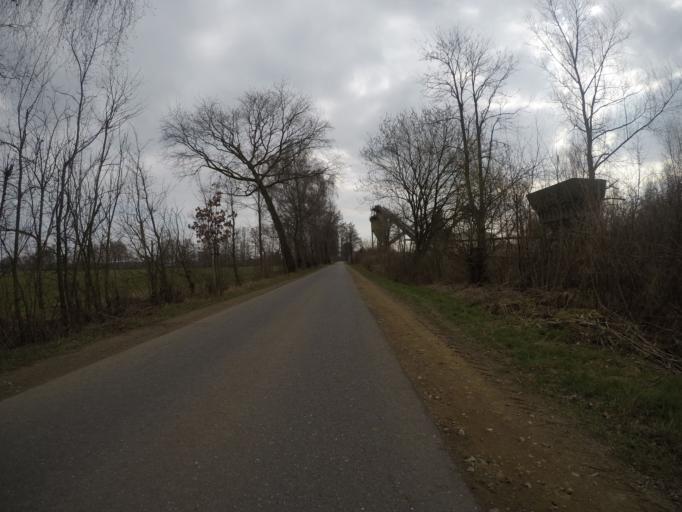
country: DE
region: North Rhine-Westphalia
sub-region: Regierungsbezirk Dusseldorf
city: Hamminkeln
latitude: 51.7770
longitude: 6.5913
